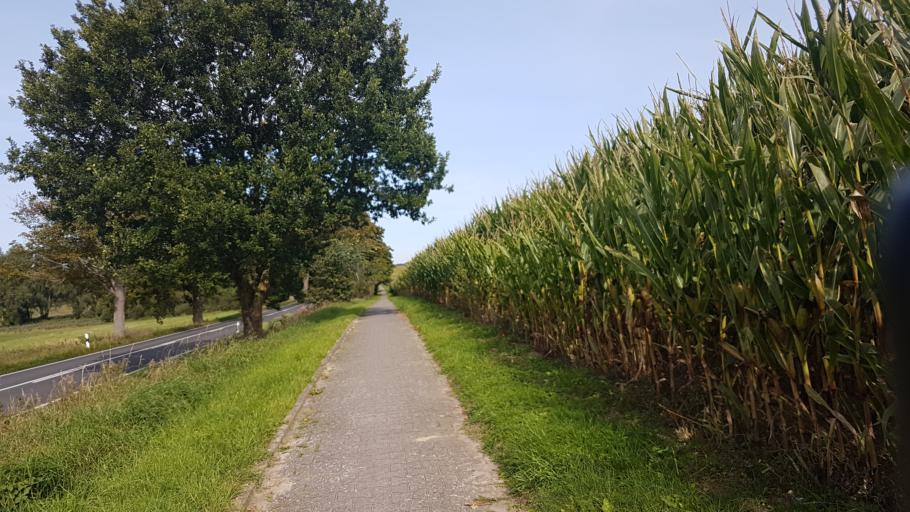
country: DE
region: Mecklenburg-Vorpommern
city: Samtens
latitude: 54.3679
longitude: 13.2909
